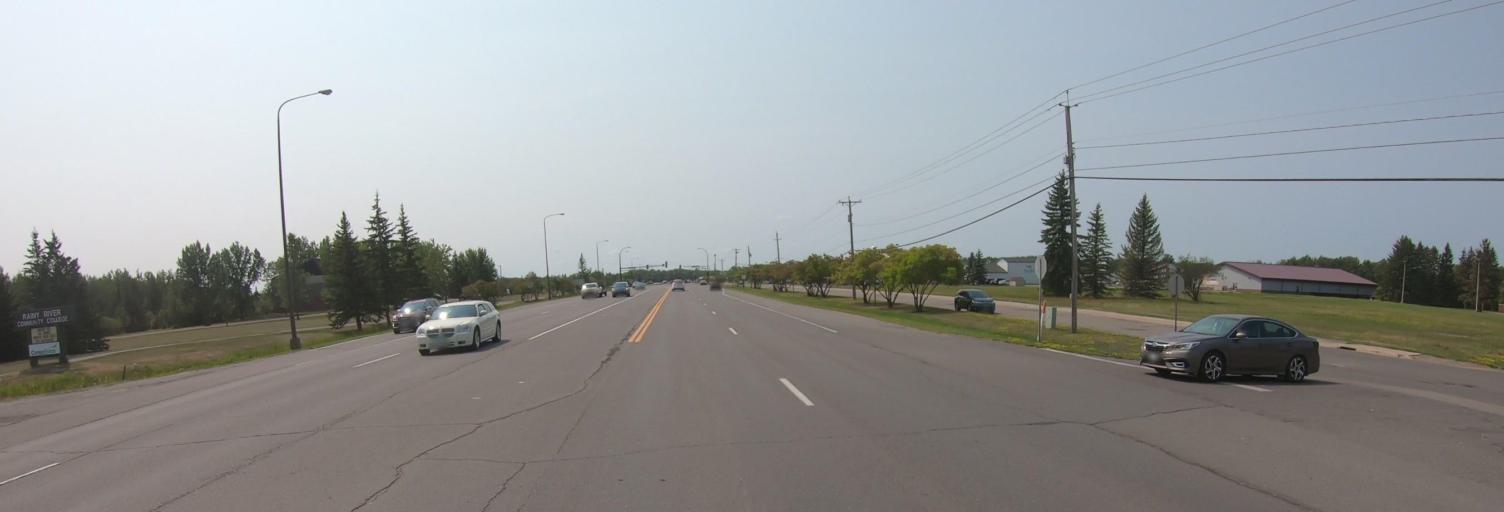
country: US
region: Minnesota
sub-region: Koochiching County
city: International Falls
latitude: 48.5916
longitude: -93.4342
